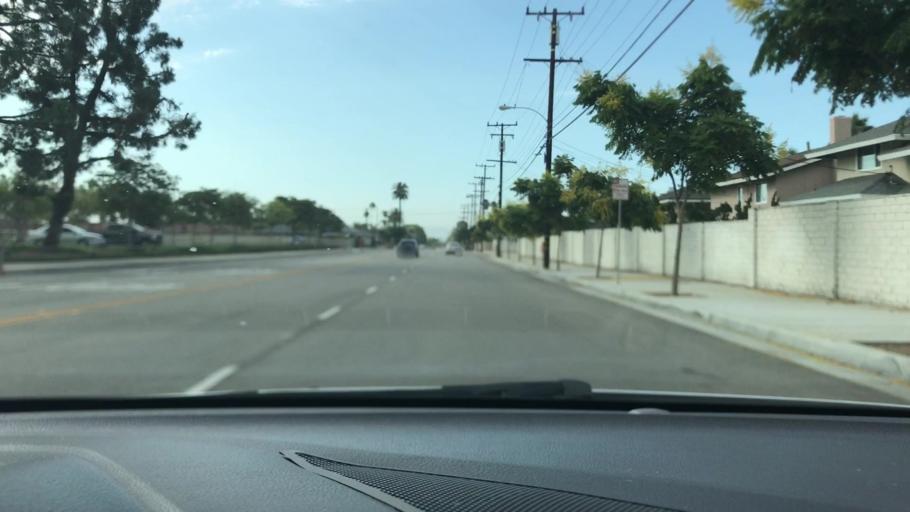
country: US
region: California
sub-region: Orange County
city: North Tustin
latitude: 33.7832
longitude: -117.8184
